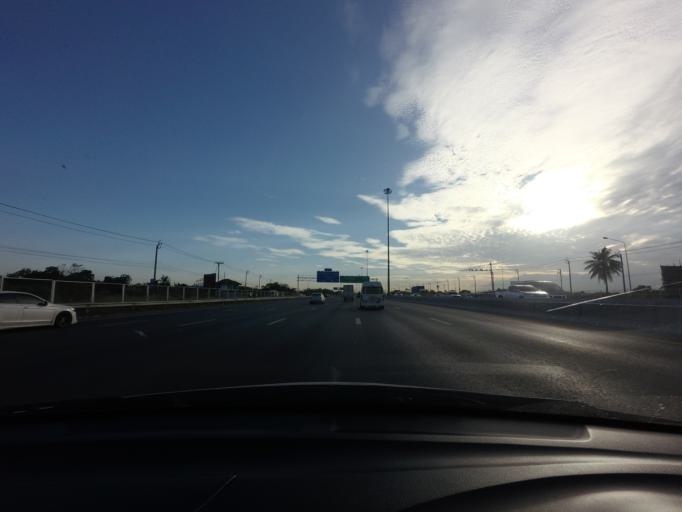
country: TH
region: Pathum Thani
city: Lam Luk Ka
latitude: 13.9132
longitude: 100.7016
